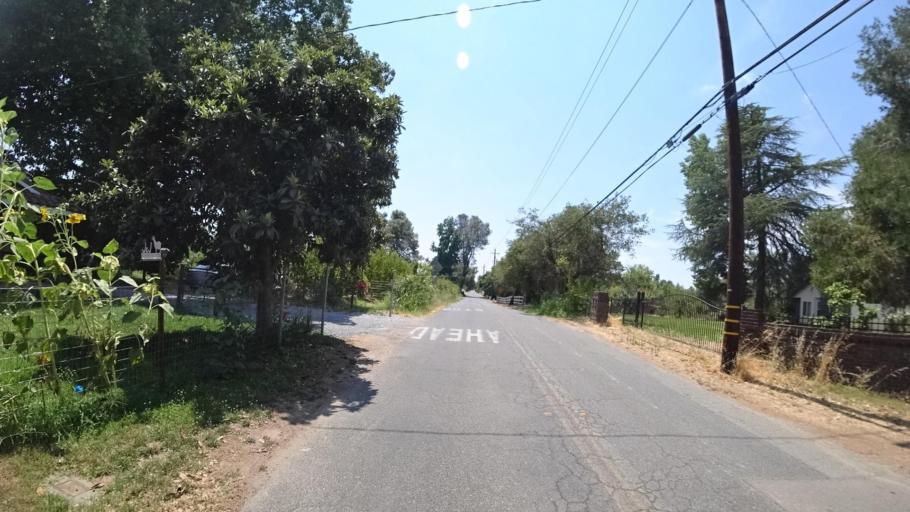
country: US
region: California
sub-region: Placer County
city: Loomis
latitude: 38.8233
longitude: -121.2195
